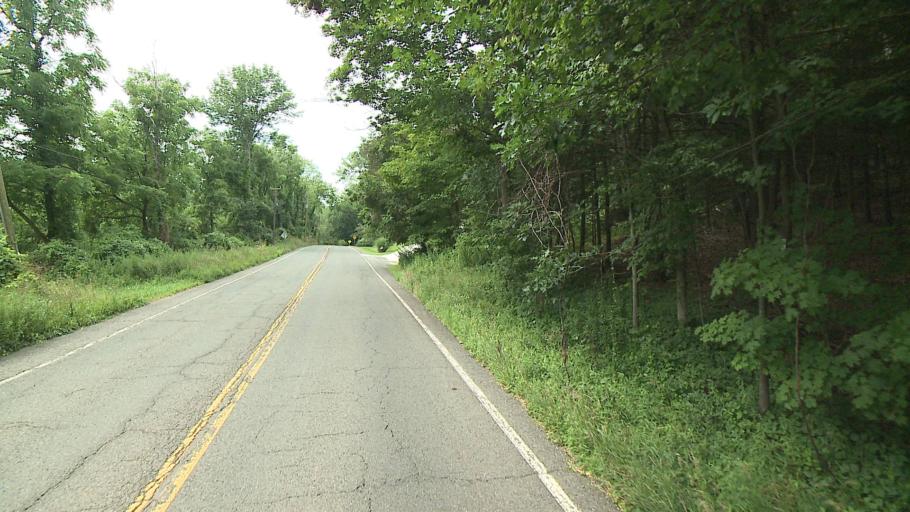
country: US
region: Connecticut
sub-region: Fairfield County
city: Sherman
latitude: 41.6467
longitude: -73.5168
